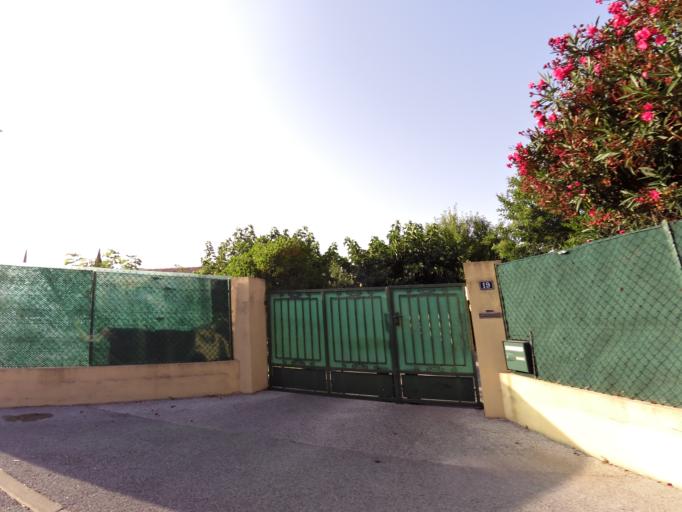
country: FR
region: Provence-Alpes-Cote d'Azur
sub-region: Departement du Var
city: Hyeres
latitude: 43.1185
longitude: 6.1384
